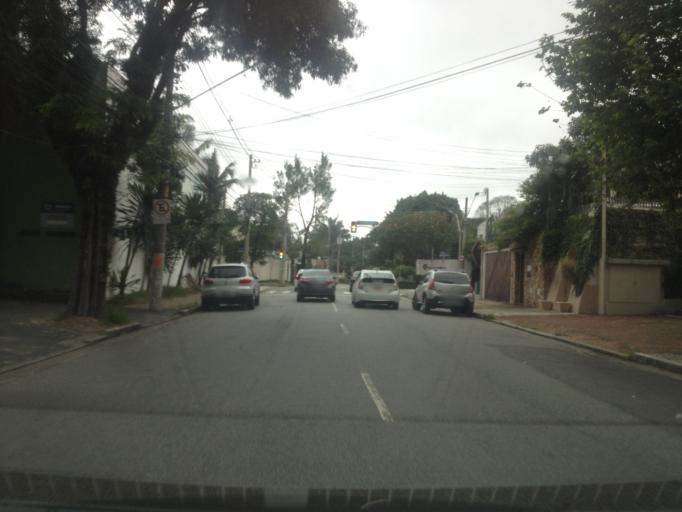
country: BR
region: Sao Paulo
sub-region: Sao Paulo
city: Sao Paulo
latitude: -23.5681
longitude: -46.6781
